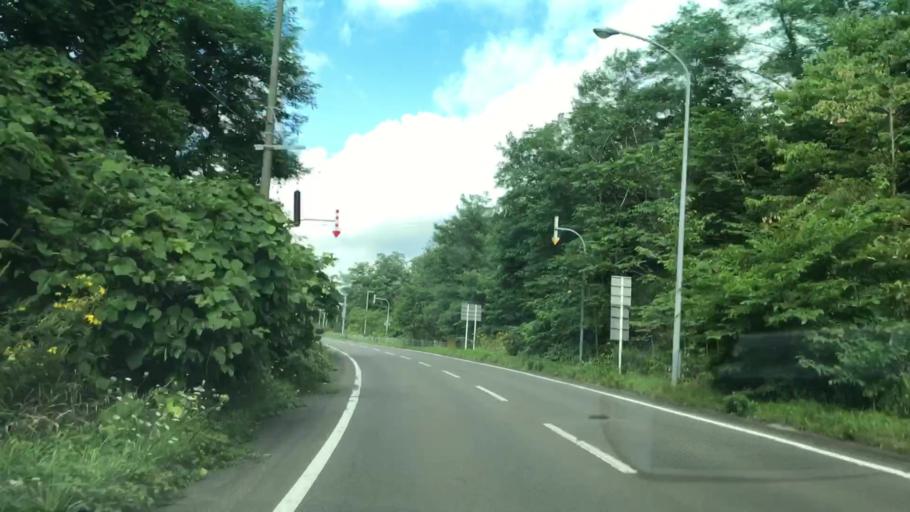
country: JP
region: Hokkaido
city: Muroran
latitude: 42.3663
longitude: 140.9534
